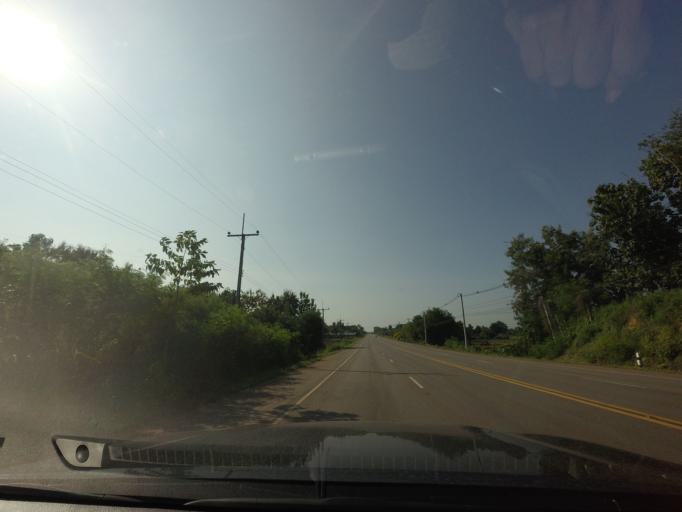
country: TH
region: Phetchabun
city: Lom Kao
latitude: 16.8306
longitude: 101.1807
